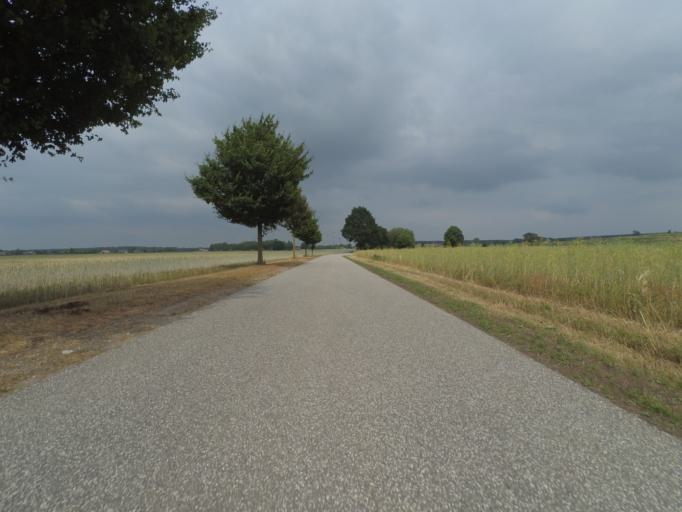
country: DE
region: Mecklenburg-Vorpommern
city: Plau am See
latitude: 53.4235
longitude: 12.1510
